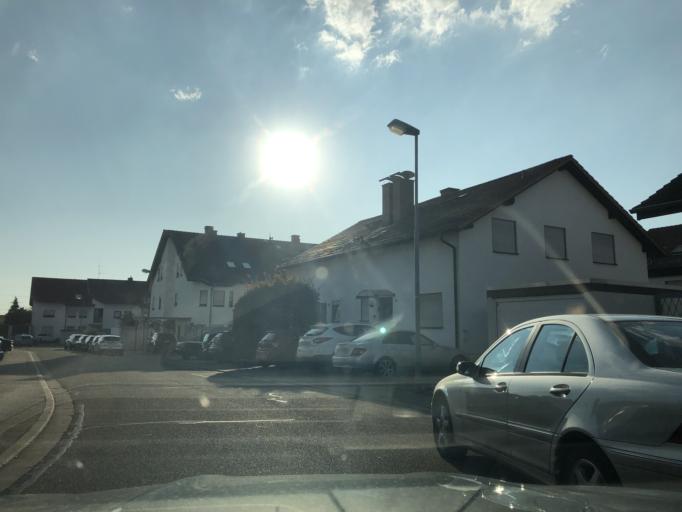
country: DE
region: Baden-Wuerttemberg
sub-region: Karlsruhe Region
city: Leimen
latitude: 49.3532
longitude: 8.6796
